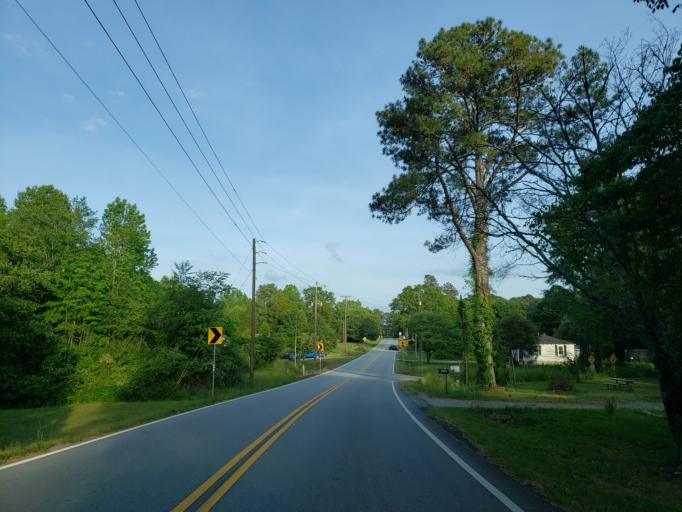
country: US
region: Georgia
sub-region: Carroll County
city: Carrollton
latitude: 33.5918
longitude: -85.1234
